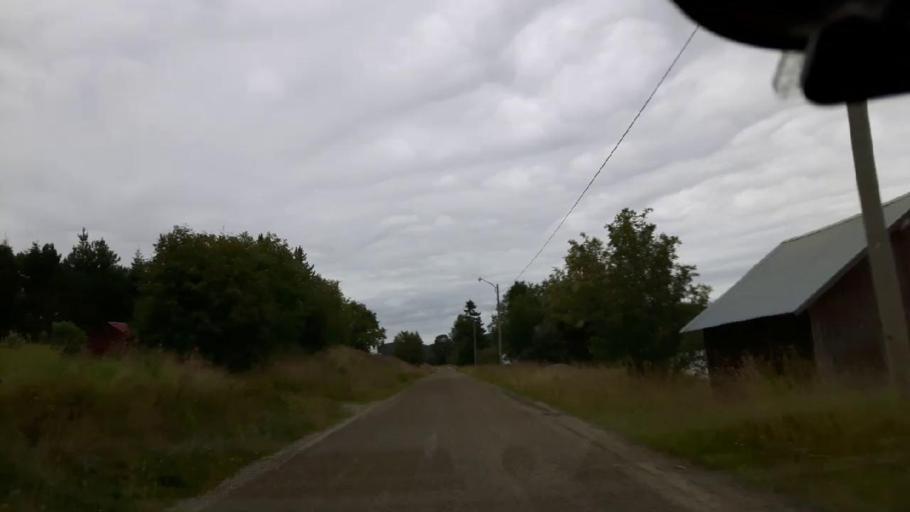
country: SE
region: Jaemtland
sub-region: Braecke Kommun
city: Braecke
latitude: 62.9960
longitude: 15.3824
